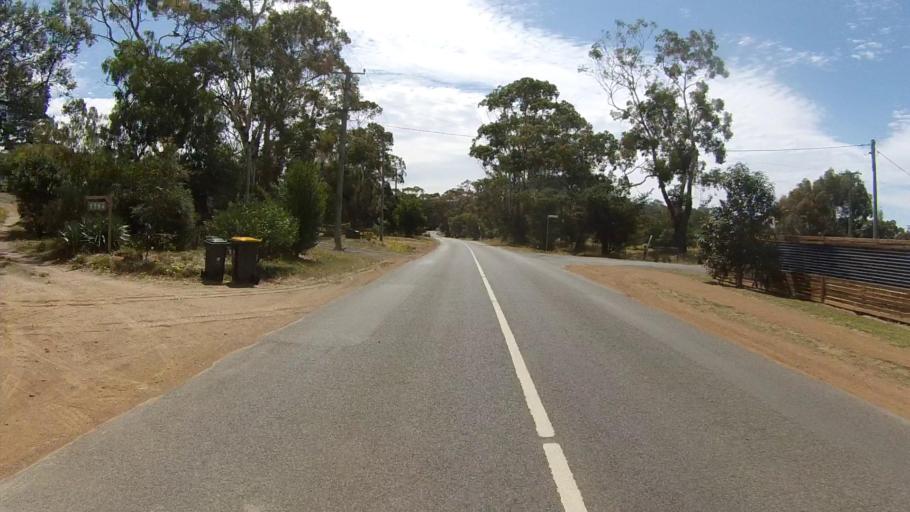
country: AU
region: Tasmania
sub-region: Kingborough
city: Blackmans Bay
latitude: -43.0241
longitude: 147.4180
